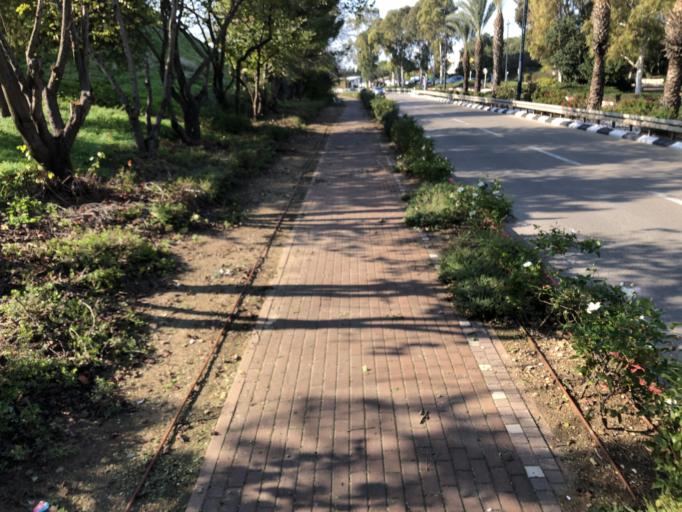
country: IL
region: Northern District
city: `Akko
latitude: 32.9226
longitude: 35.0892
